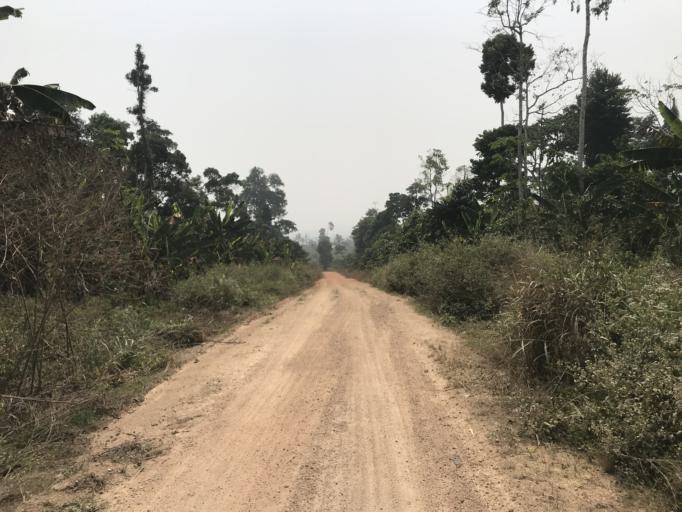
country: NG
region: Osun
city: Ifetedo
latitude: 7.0456
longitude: 4.4777
